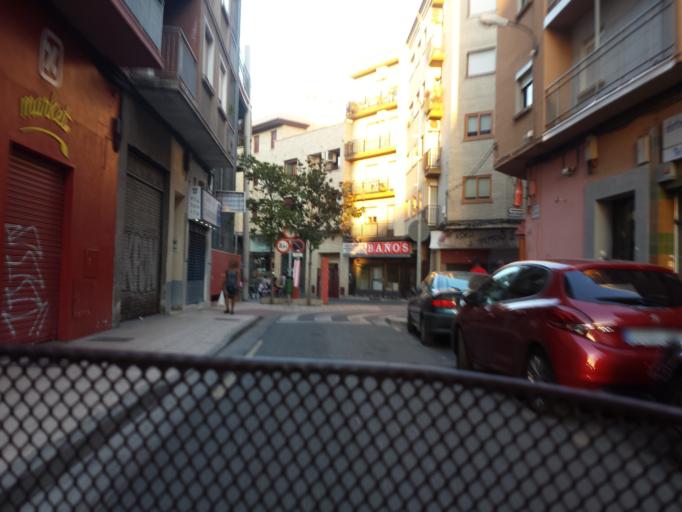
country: ES
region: Aragon
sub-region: Provincia de Zaragoza
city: Delicias
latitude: 41.6505
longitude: -0.9057
